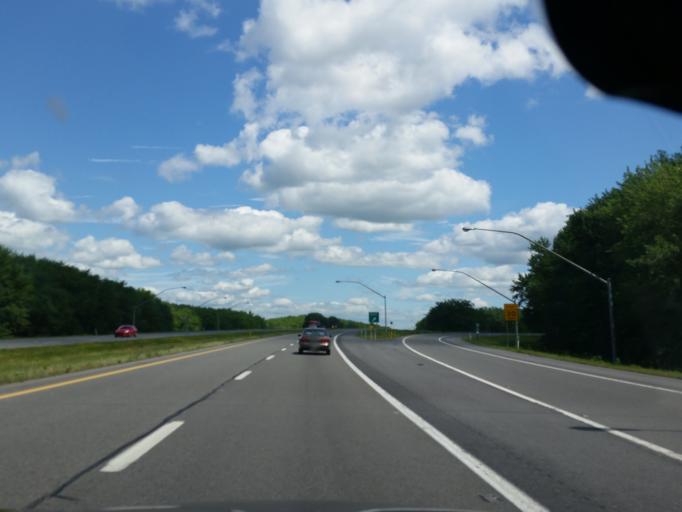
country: US
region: Pennsylvania
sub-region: Snyder County
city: Selinsgrove
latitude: 40.7814
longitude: -76.8653
